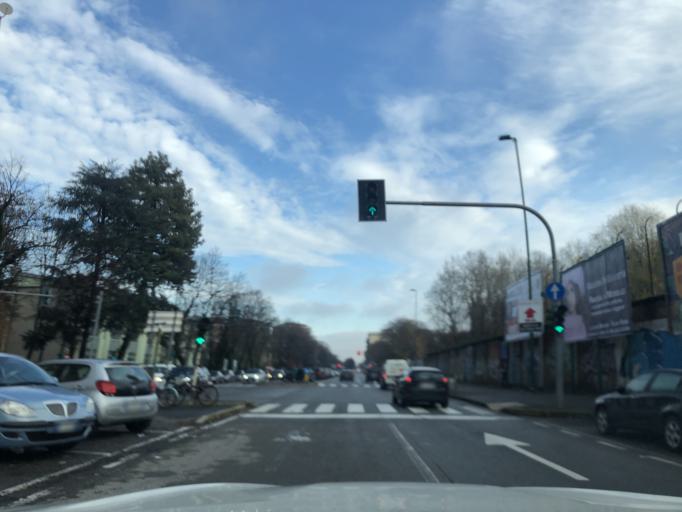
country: IT
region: Lombardy
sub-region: Citta metropolitana di Milano
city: Sesto San Giovanni
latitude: 45.5339
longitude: 9.2425
